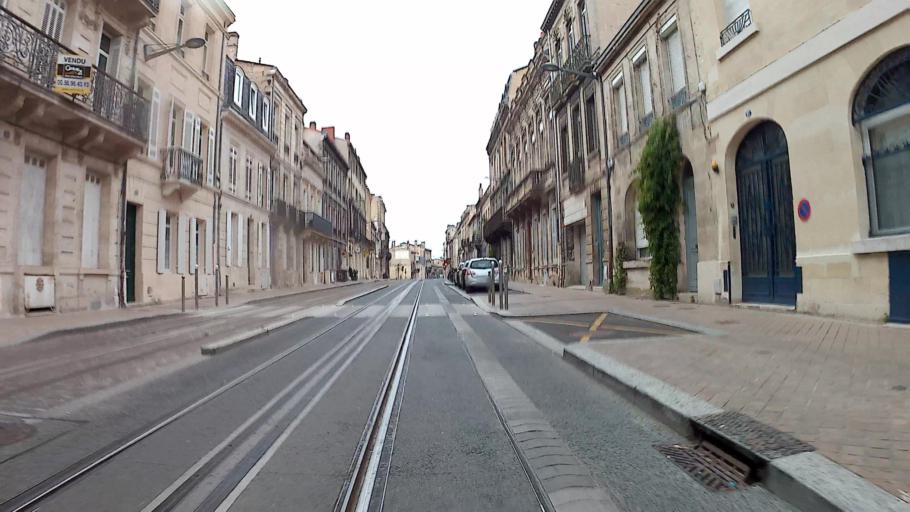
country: FR
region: Aquitaine
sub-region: Departement de la Gironde
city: Bordeaux
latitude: 44.8510
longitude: -0.5884
